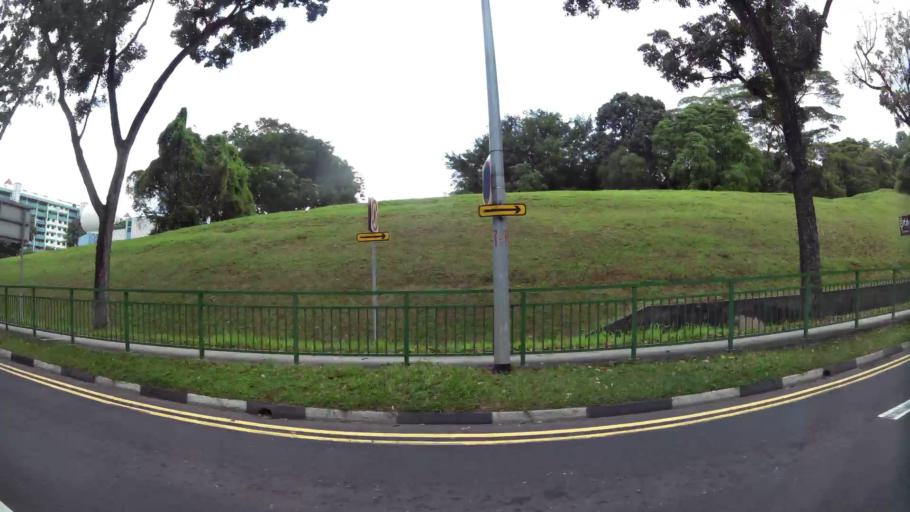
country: MY
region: Johor
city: Johor Bahru
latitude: 1.4401
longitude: 103.7711
